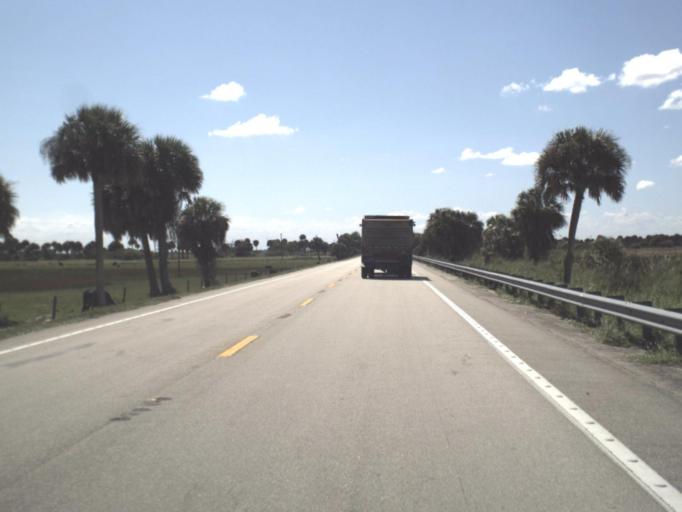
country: US
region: Florida
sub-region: Glades County
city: Buckhead Ridge
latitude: 27.0988
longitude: -80.9529
